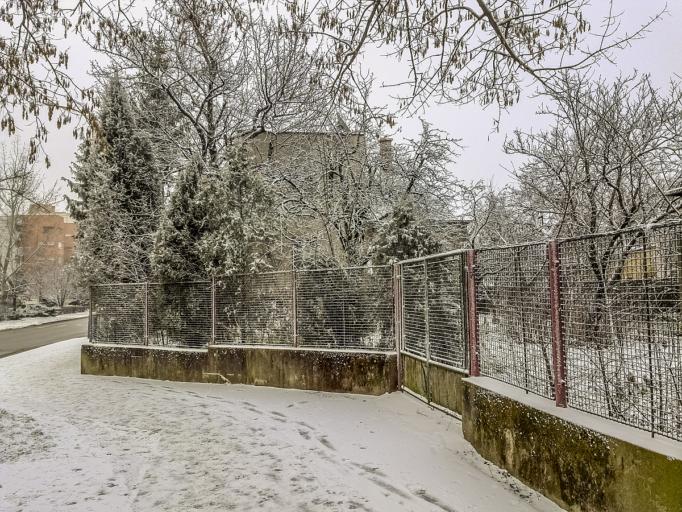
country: SK
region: Kosicky
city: Kosice
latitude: 48.7102
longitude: 21.2393
